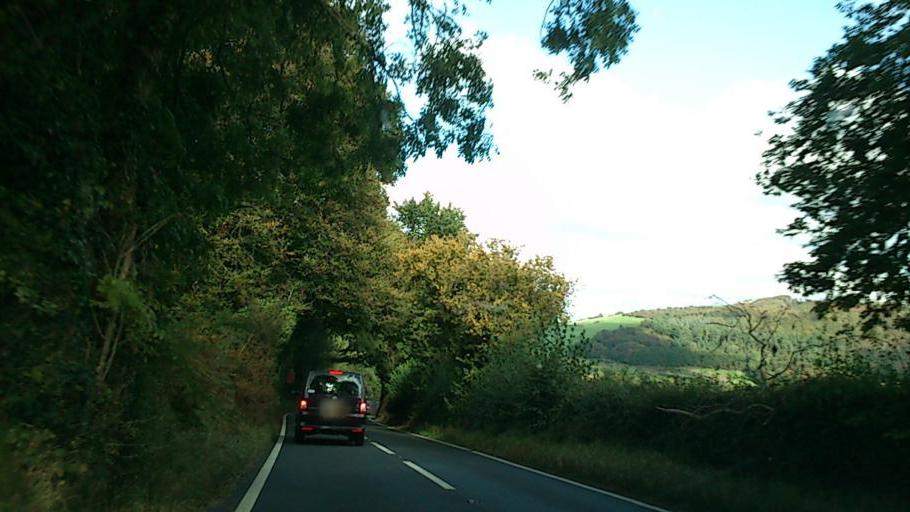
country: GB
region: Wales
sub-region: County of Ceredigion
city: Bow Street
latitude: 52.4292
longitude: -4.0322
